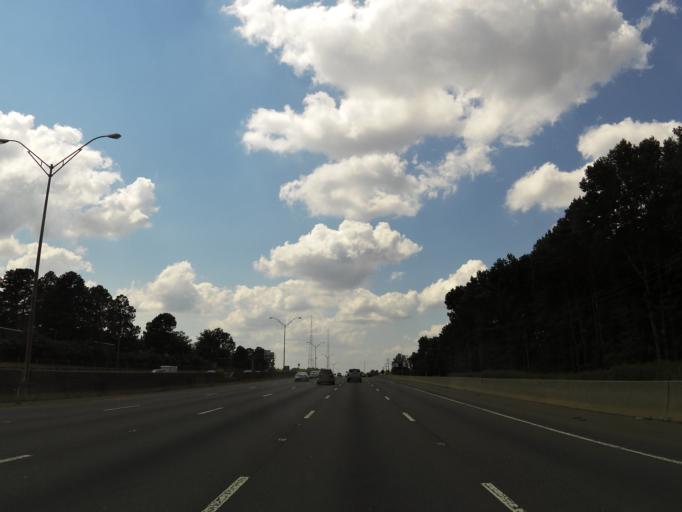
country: US
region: North Carolina
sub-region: Mecklenburg County
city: Charlotte
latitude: 35.2809
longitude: -80.7864
